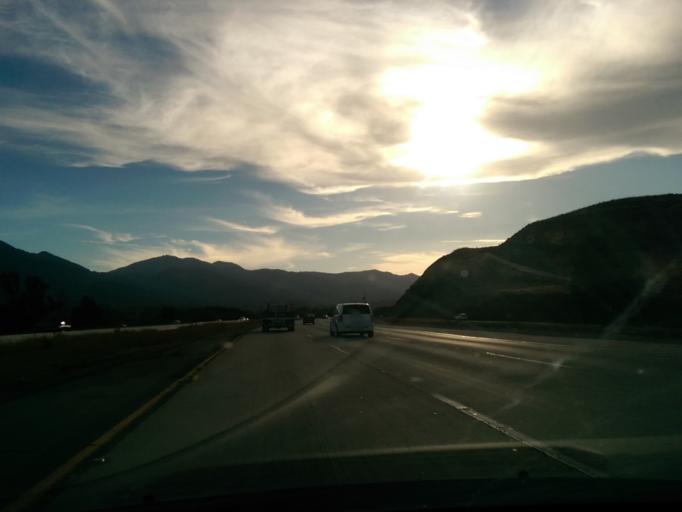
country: US
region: California
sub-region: Riverside County
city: Lake Elsinore
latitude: 33.7301
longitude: -117.3938
